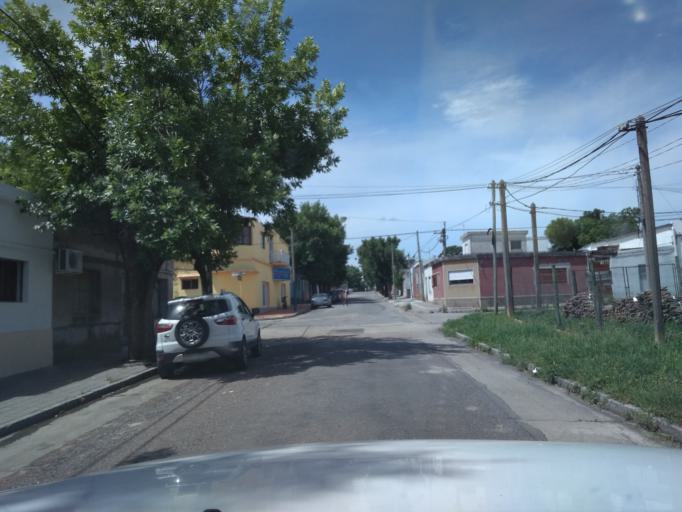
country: UY
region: Florida
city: Florida
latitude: -34.1037
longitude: -56.2156
